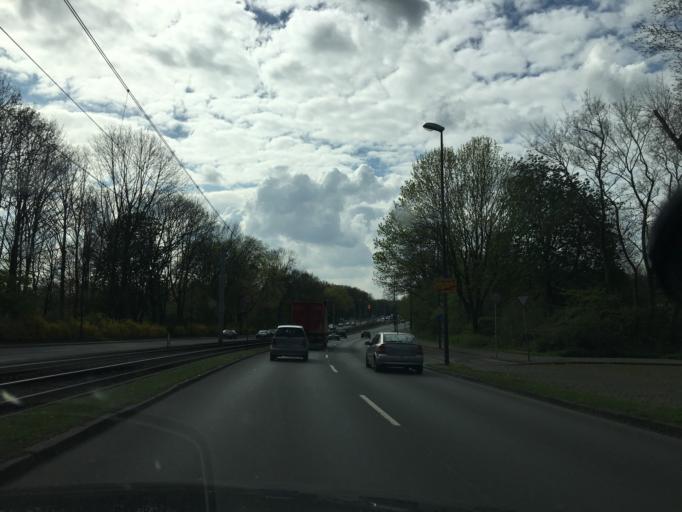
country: DE
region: North Rhine-Westphalia
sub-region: Regierungsbezirk Munster
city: Gladbeck
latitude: 51.5673
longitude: 7.0577
